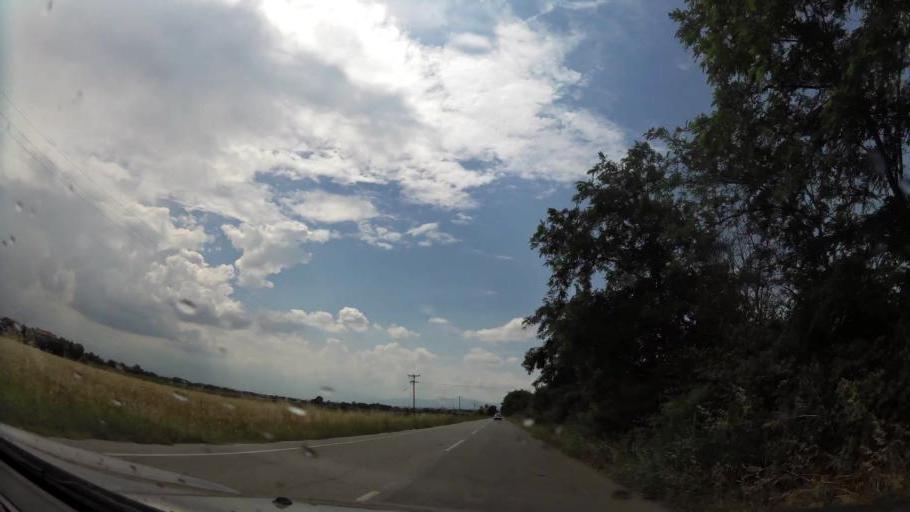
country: GR
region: Central Macedonia
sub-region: Nomos Pierias
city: Korinos
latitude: 40.3098
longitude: 22.6066
